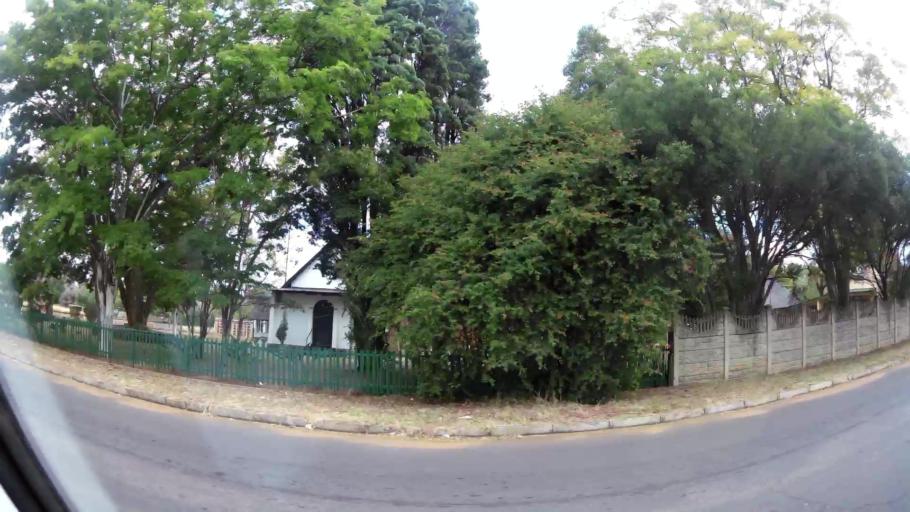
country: ZA
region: Limpopo
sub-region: Waterberg District Municipality
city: Modimolle
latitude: -24.7041
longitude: 28.4067
